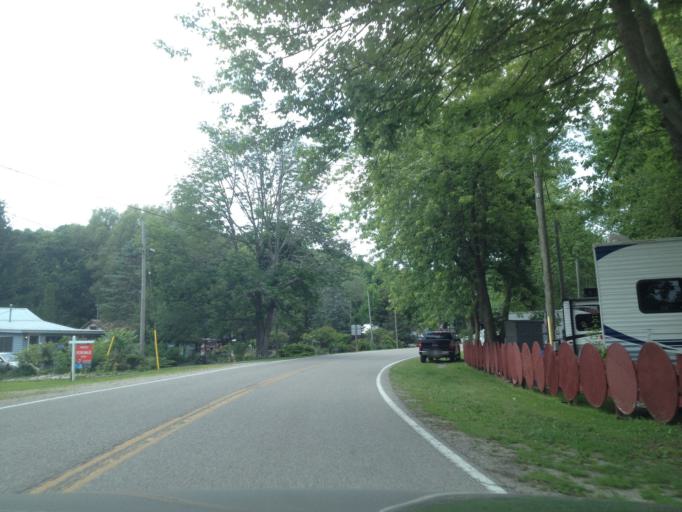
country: CA
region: Ontario
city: Aylmer
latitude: 42.6560
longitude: -81.0151
